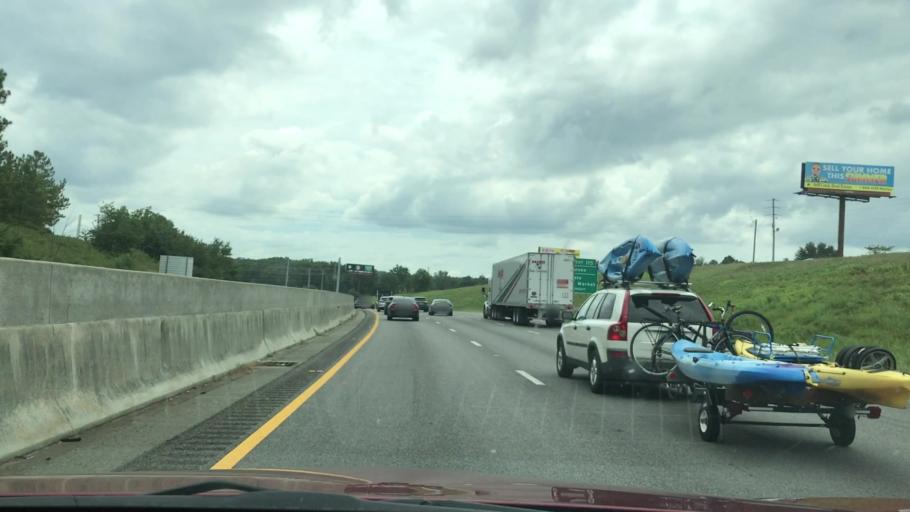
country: US
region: South Carolina
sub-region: Lexington County
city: Springdale
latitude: 33.9426
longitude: -81.0889
